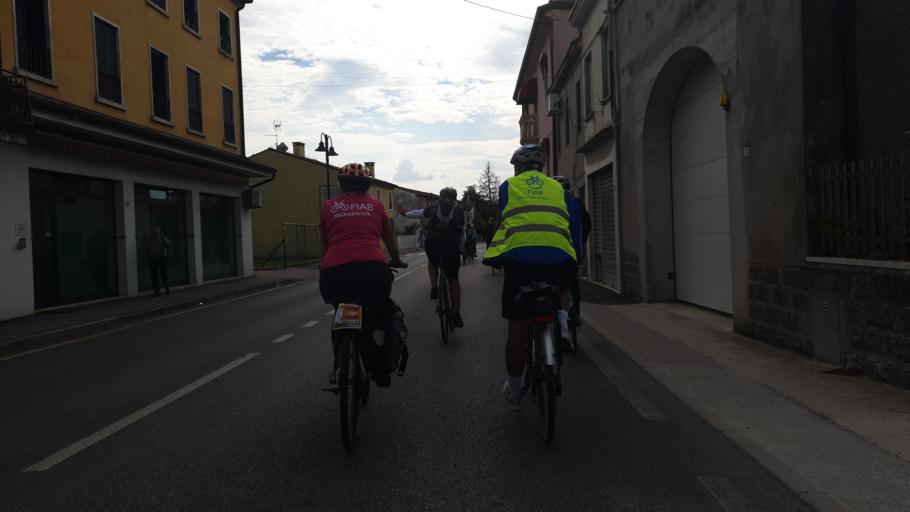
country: IT
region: Veneto
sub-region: Provincia di Vicenza
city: Poiana Maggiore
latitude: 45.2879
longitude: 11.4999
